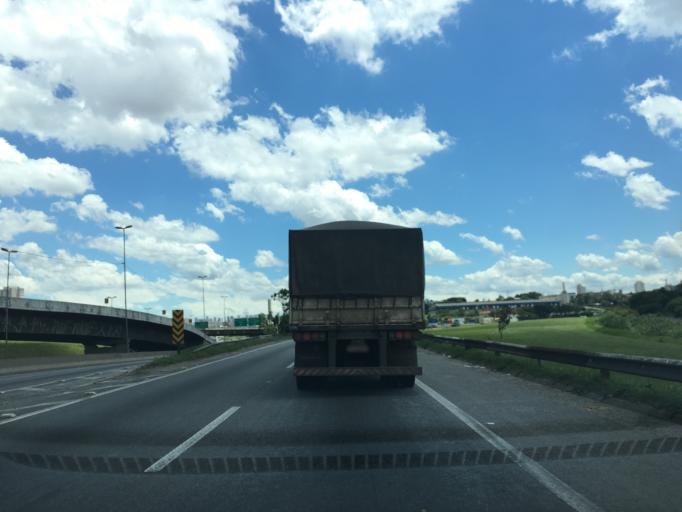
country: BR
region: Sao Paulo
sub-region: Guarulhos
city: Guarulhos
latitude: -23.4959
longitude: -46.5597
